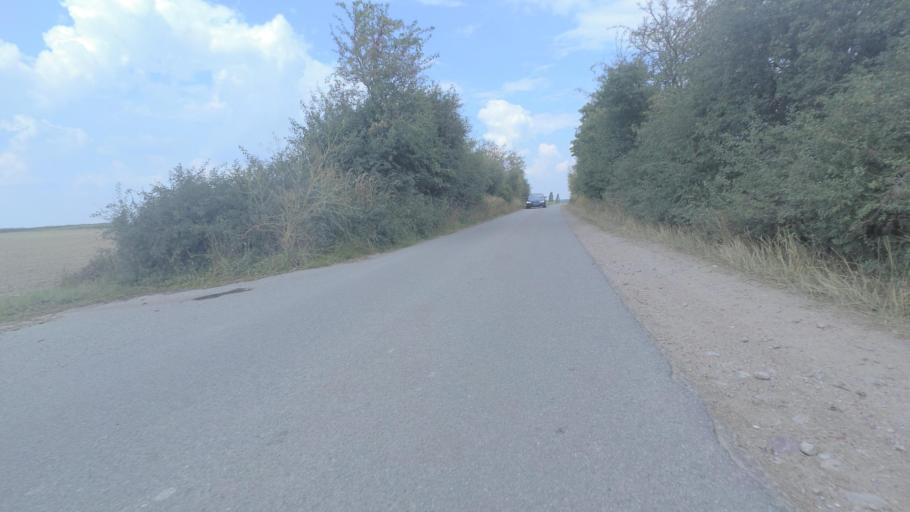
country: DE
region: Mecklenburg-Vorpommern
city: Borrentin
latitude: 53.8303
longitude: 12.9311
